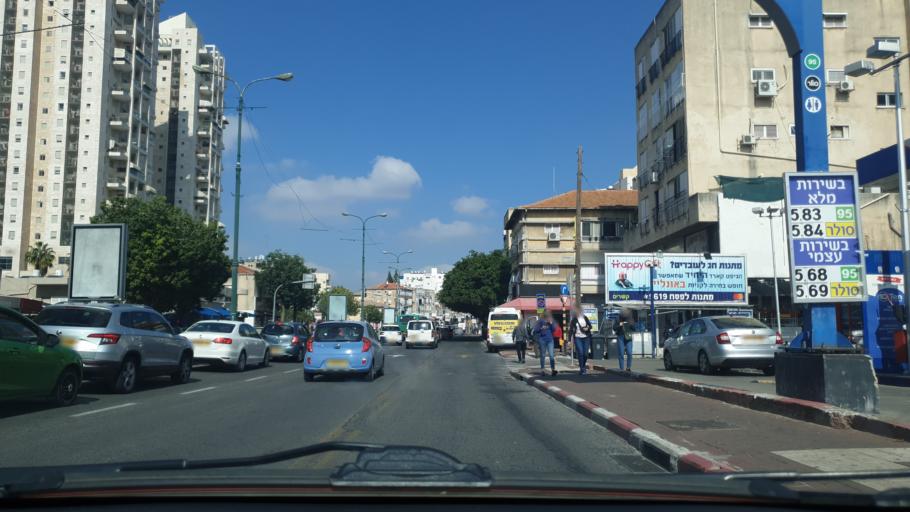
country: IL
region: Central District
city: Rishon LeZiyyon
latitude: 31.9647
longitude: 34.8030
